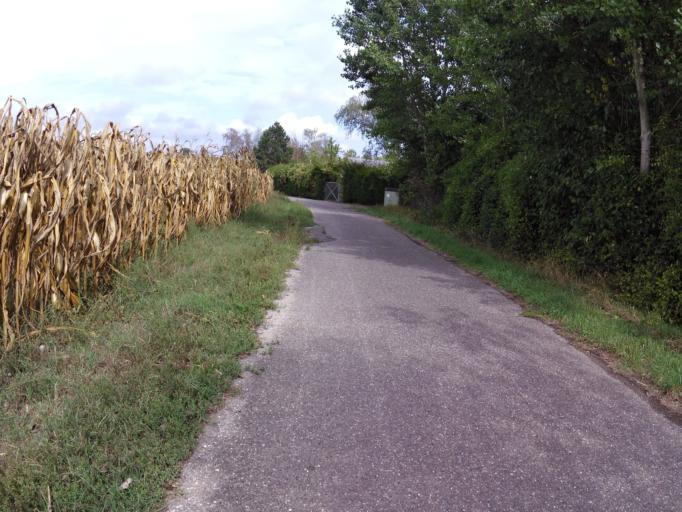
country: FR
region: Alsace
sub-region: Departement du Haut-Rhin
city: Biesheim
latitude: 48.0443
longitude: 7.5543
